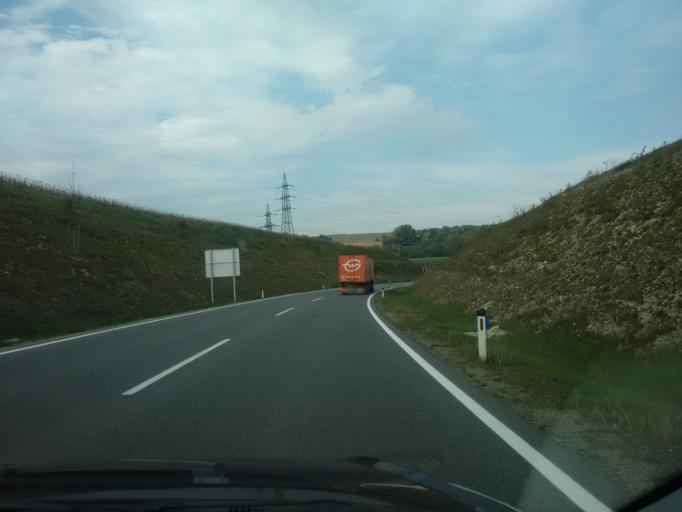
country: AT
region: Upper Austria
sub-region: Wels-Land
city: Stadl-Paura
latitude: 48.0930
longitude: 13.8526
